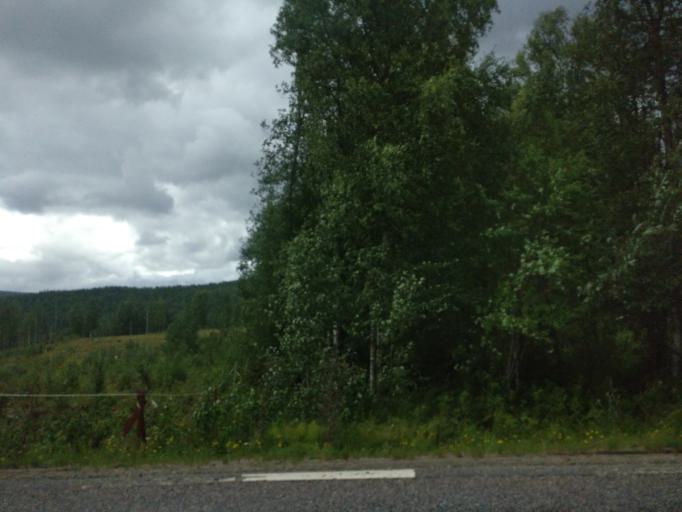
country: SE
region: Vaermland
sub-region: Torsby Kommun
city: Torsby
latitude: 60.7725
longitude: 12.7525
